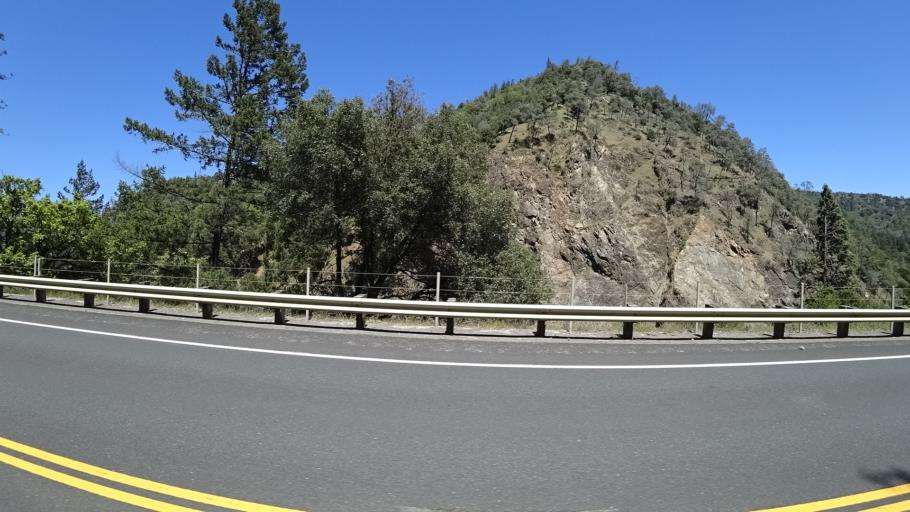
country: US
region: California
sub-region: Humboldt County
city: Willow Creek
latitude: 40.7901
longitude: -123.4518
